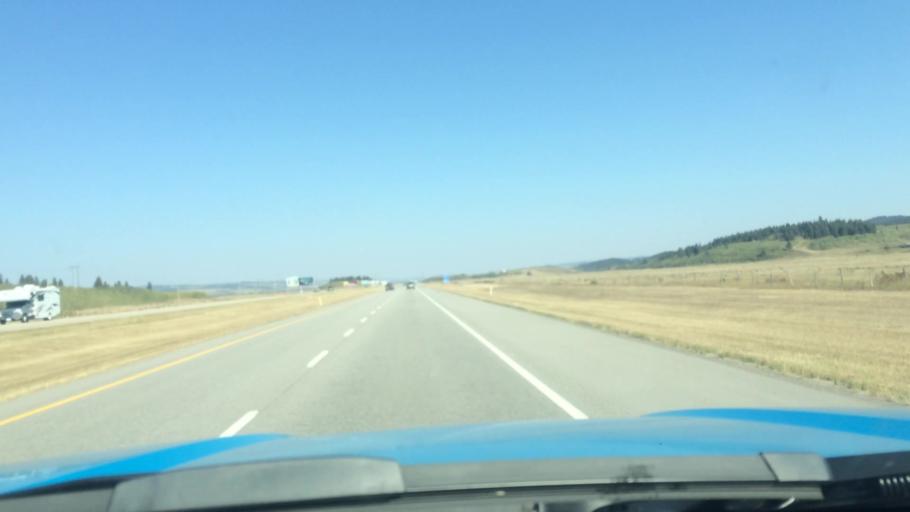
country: CA
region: Alberta
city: Canmore
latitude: 51.1154
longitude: -114.9909
